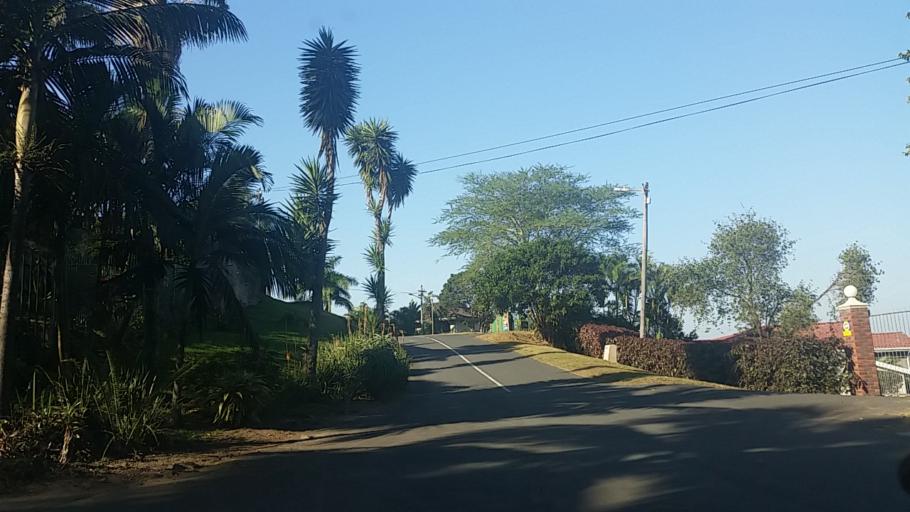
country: ZA
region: KwaZulu-Natal
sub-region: eThekwini Metropolitan Municipality
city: Berea
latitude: -29.8468
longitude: 30.9123
